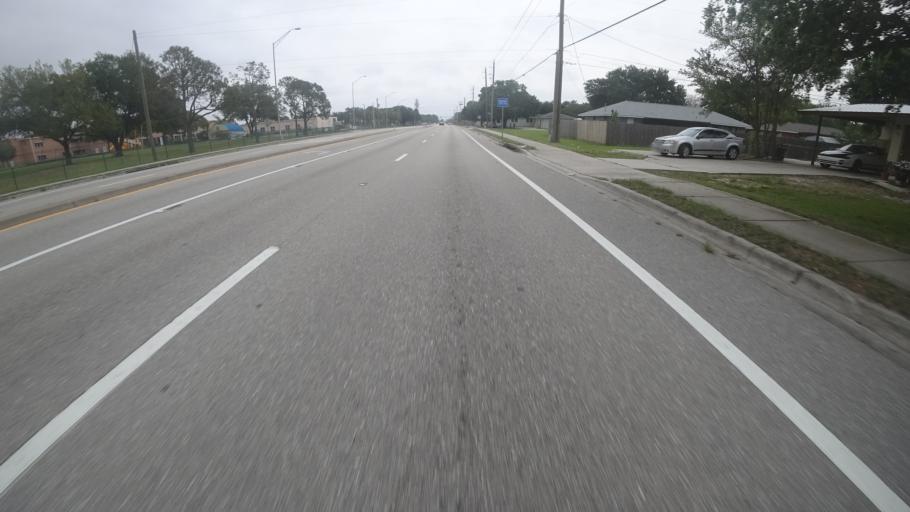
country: US
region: Florida
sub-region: Manatee County
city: Whitfield
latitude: 27.4293
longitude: -82.5584
